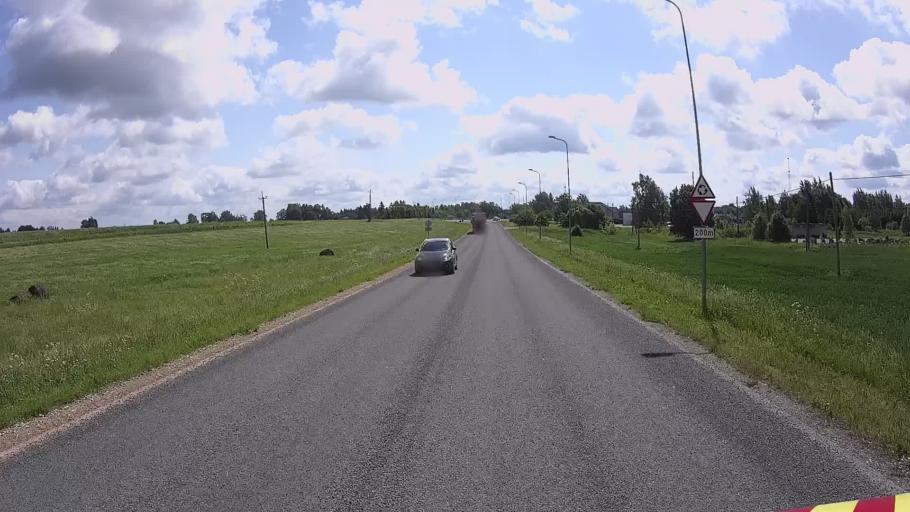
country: EE
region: Viljandimaa
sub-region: Viiratsi vald
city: Viiratsi
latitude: 58.2462
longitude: 25.8502
